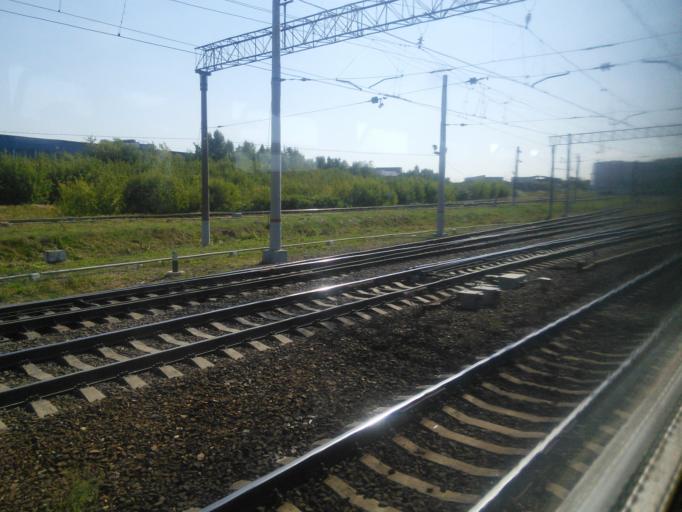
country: RU
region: Moskovskaya
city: Biryulevo Zapadnoye
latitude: 55.5976
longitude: 37.6249
